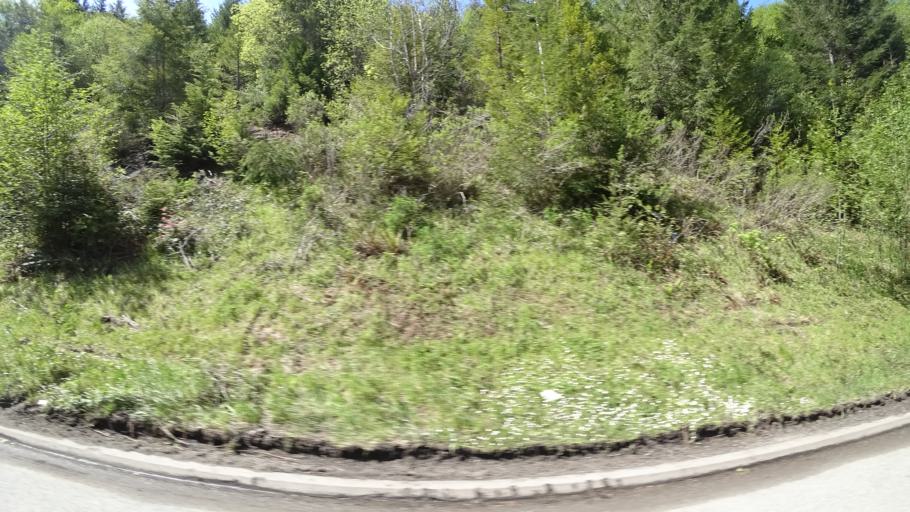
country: US
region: California
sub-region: Del Norte County
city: Bertsch-Oceanview
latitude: 41.4274
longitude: -124.0098
